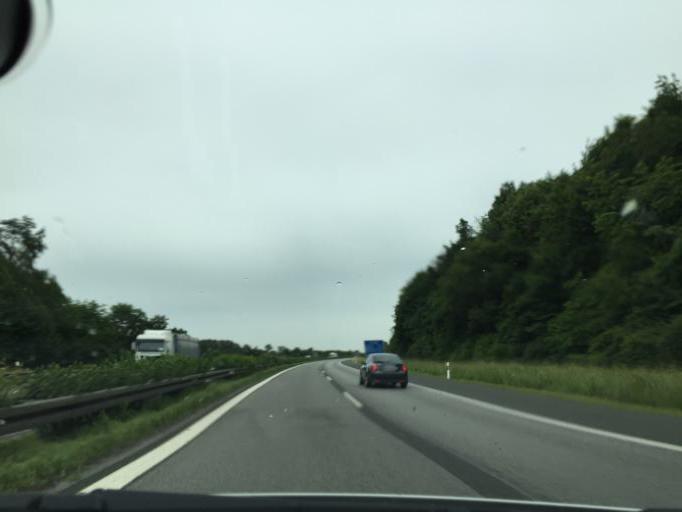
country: DE
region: Bavaria
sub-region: Regierungsbezirk Unterfranken
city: Gadheim
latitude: 50.0184
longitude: 10.3340
